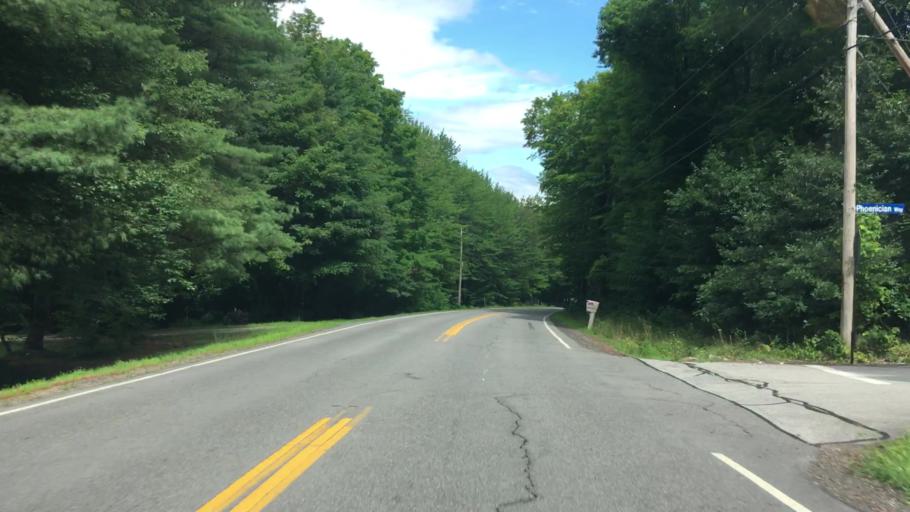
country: US
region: New Hampshire
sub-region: Belknap County
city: Meredith
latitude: 43.5874
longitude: -71.5176
